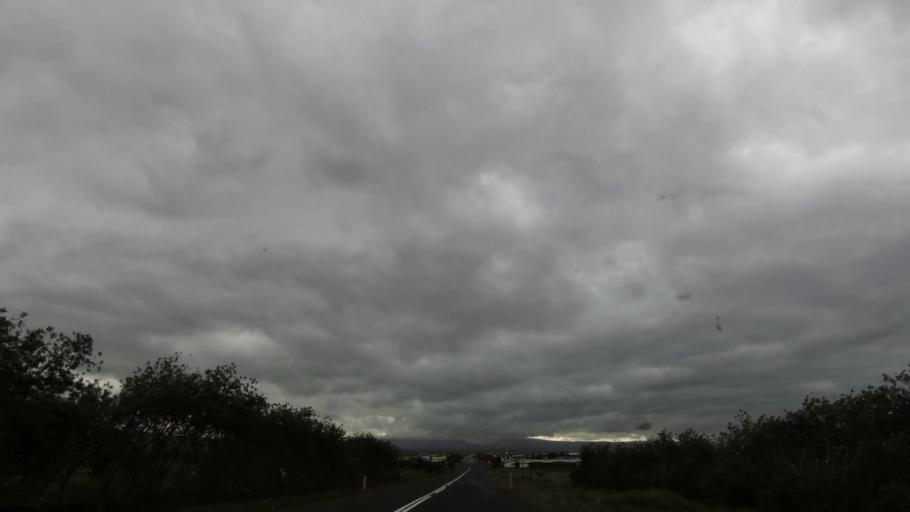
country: IS
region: West
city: Borgarnes
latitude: 65.1150
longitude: -21.7552
